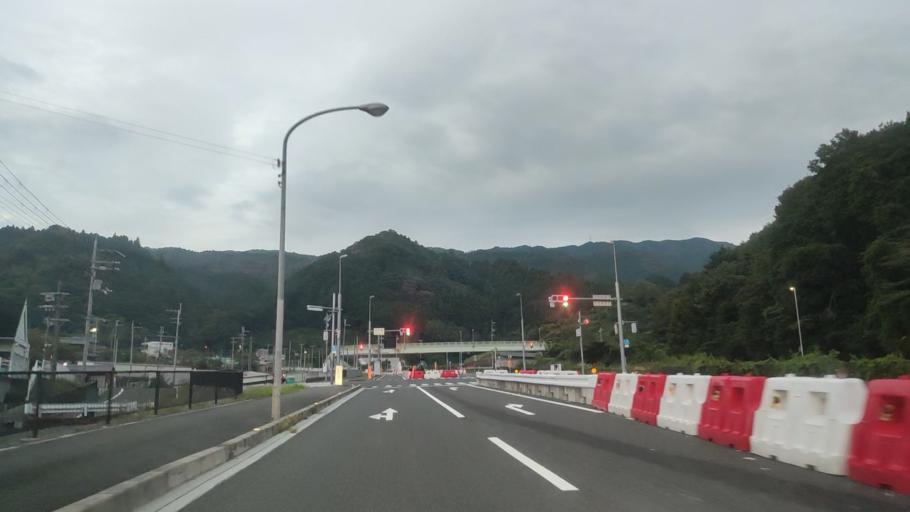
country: JP
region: Wakayama
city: Hashimoto
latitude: 34.3677
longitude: 135.6073
